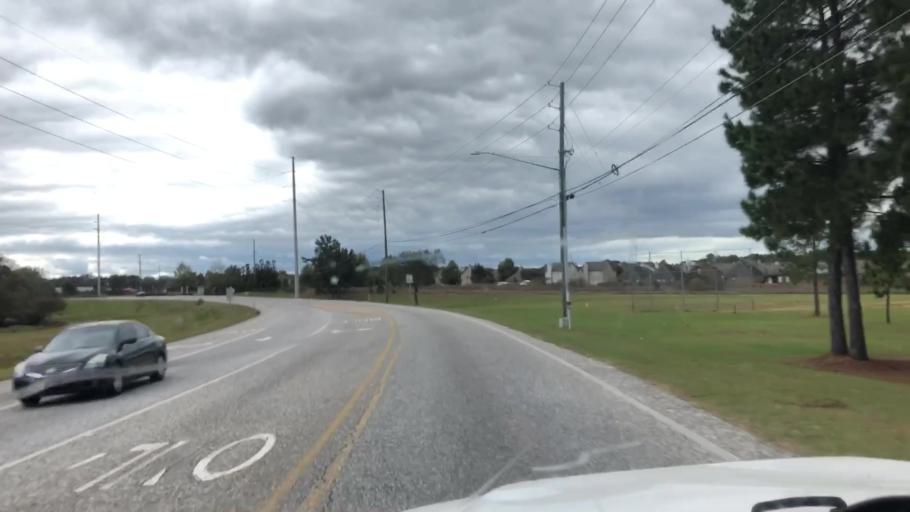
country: US
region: Alabama
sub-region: Elmore County
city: Blue Ridge
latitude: 32.3898
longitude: -86.1789
